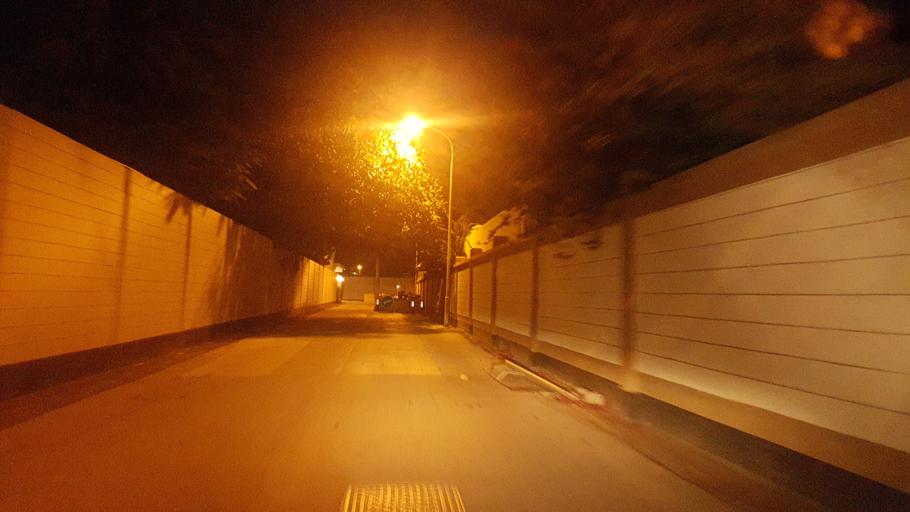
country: BH
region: Manama
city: Jidd Hafs
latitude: 26.2242
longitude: 50.4948
